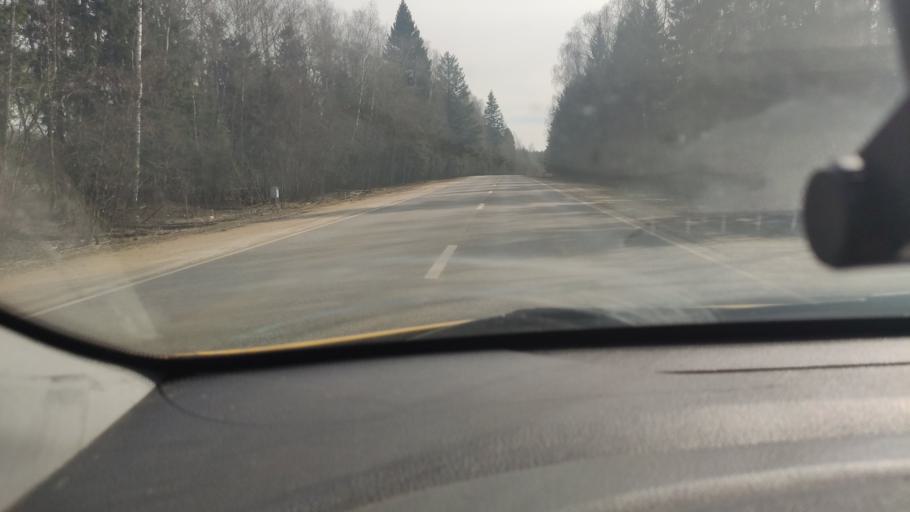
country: RU
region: Moskovskaya
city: Ruza
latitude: 55.7285
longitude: 36.1521
